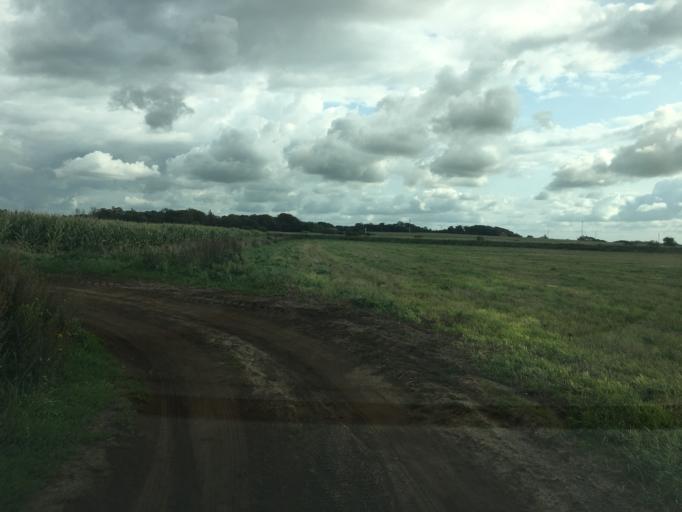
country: DK
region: South Denmark
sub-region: Tonder Kommune
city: Tonder
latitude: 54.9419
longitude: 8.9123
